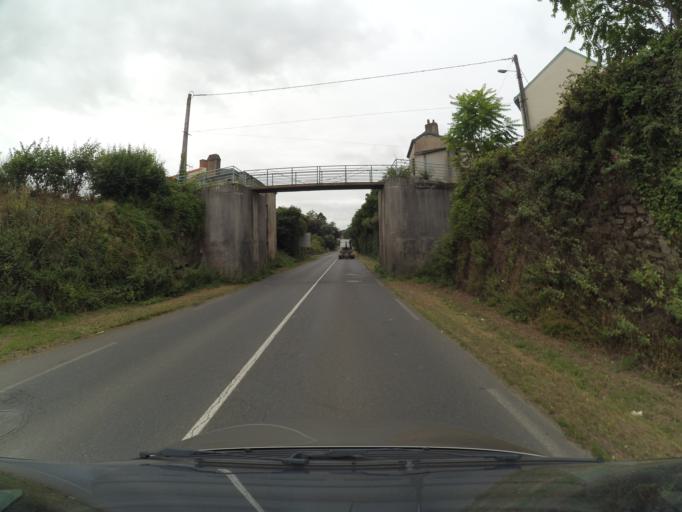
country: FR
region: Pays de la Loire
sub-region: Departement de la Vendee
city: Rocheserviere
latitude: 46.9377
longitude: -1.5142
